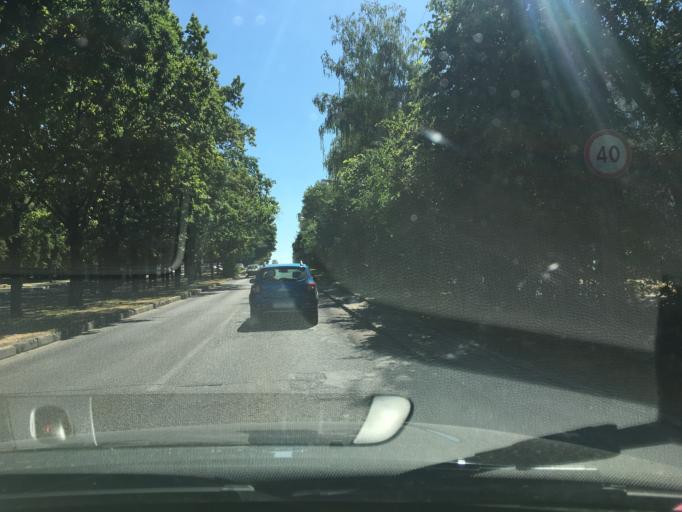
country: BY
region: Grodnenskaya
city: Hrodna
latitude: 53.6951
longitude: 23.8448
